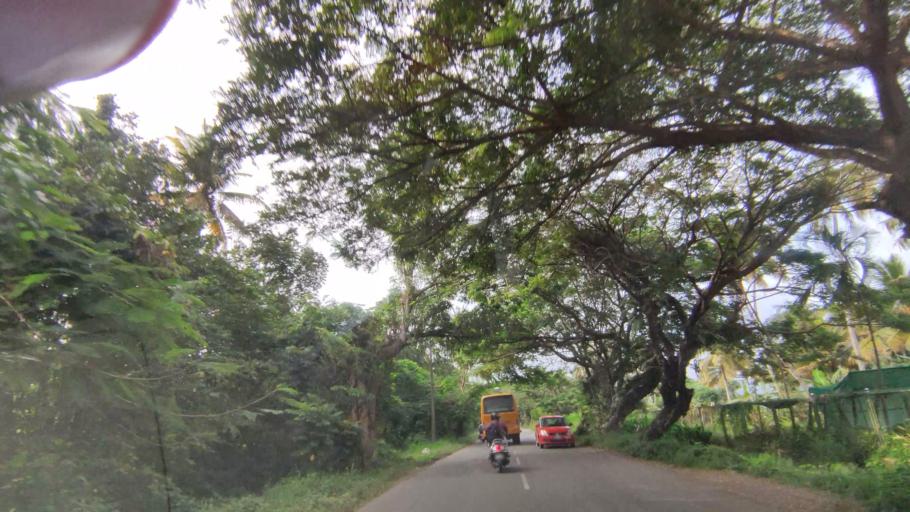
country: IN
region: Kerala
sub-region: Alappuzha
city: Shertallai
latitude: 9.6242
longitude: 76.4296
